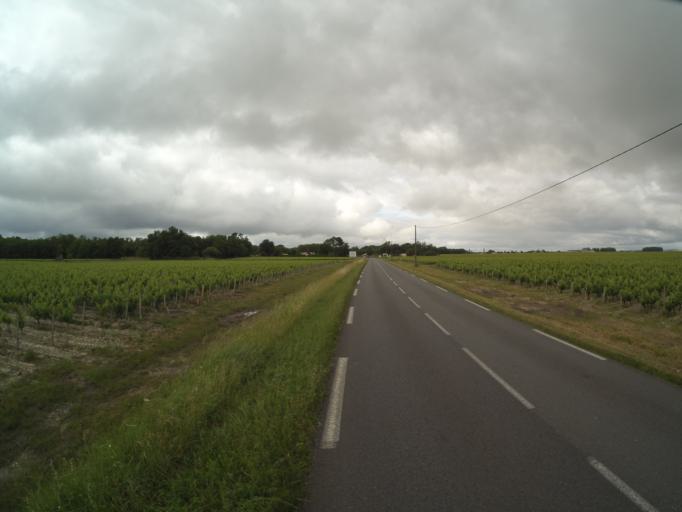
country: FR
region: Aquitaine
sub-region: Departement de la Gironde
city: Lamarque
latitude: 45.0817
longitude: -0.7274
